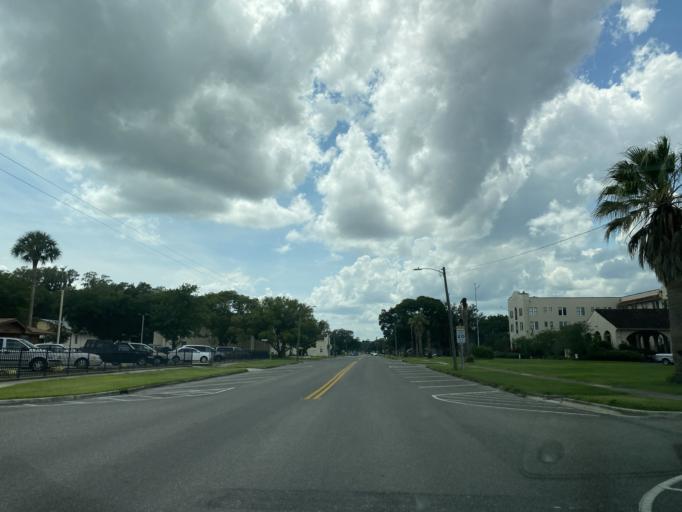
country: US
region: Florida
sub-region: Seminole County
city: Sanford
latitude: 28.8114
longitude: -81.2567
